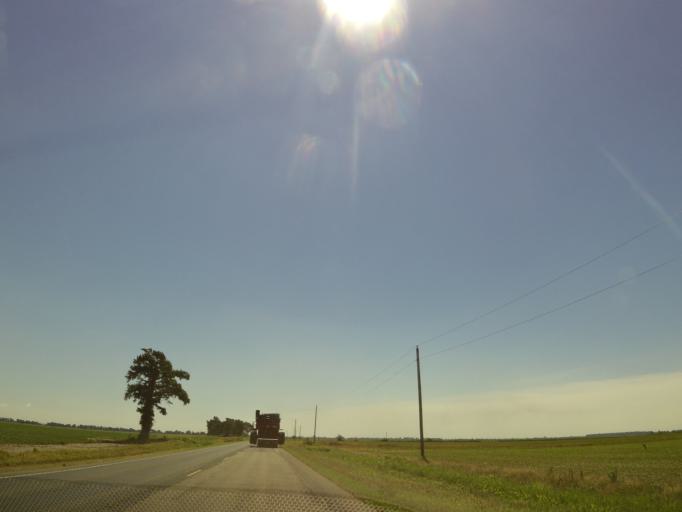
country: US
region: Missouri
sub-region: New Madrid County
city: Lilbourn
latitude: 36.5539
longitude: -89.7249
